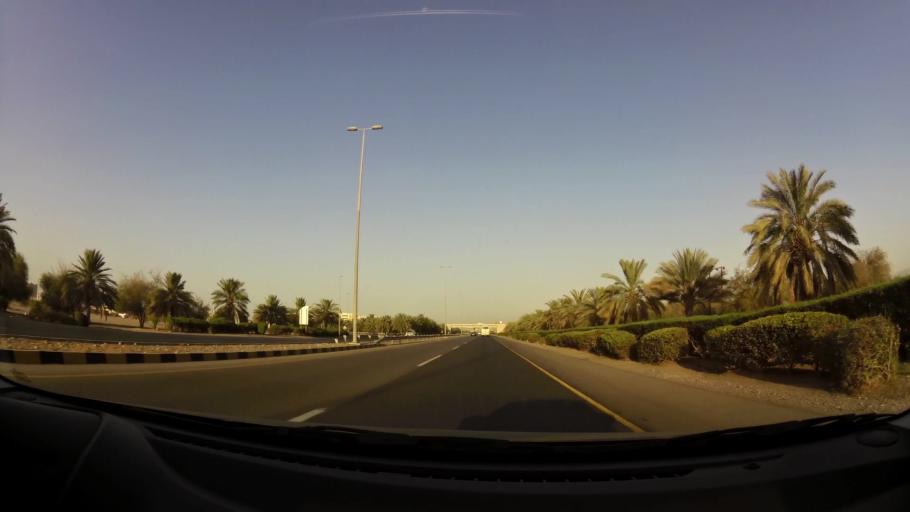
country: OM
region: Muhafazat Masqat
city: As Sib al Jadidah
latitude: 23.5917
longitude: 58.2115
